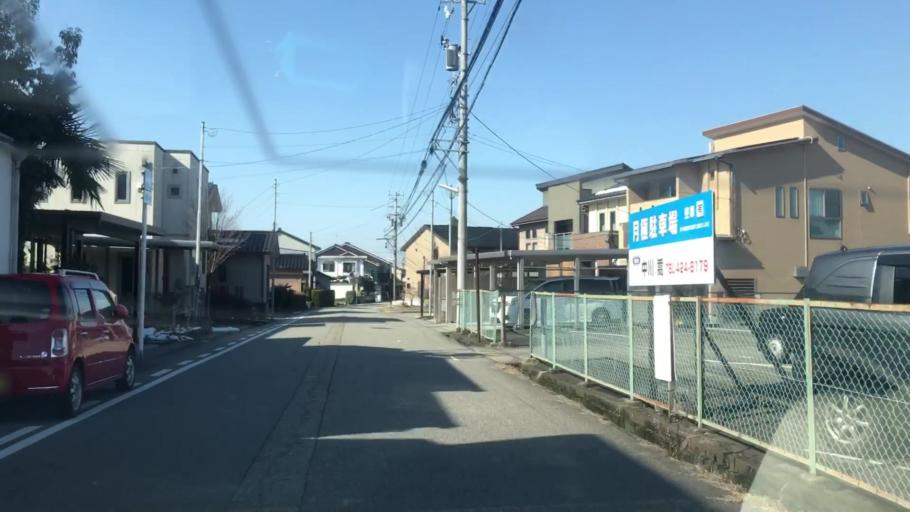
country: JP
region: Toyama
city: Toyama-shi
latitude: 36.6793
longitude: 137.2397
